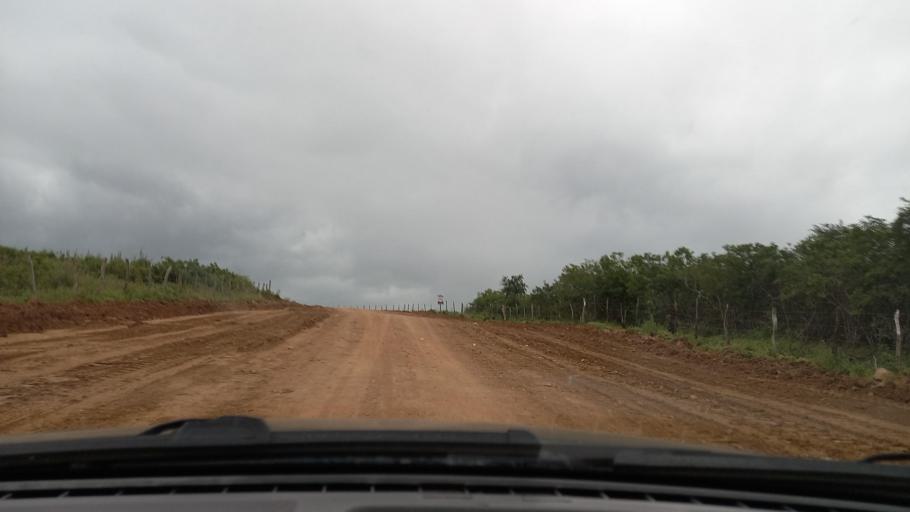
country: BR
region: Sergipe
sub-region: Caninde De Sao Francisco
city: Caninde de Sao Francisco
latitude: -9.6172
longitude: -37.7604
